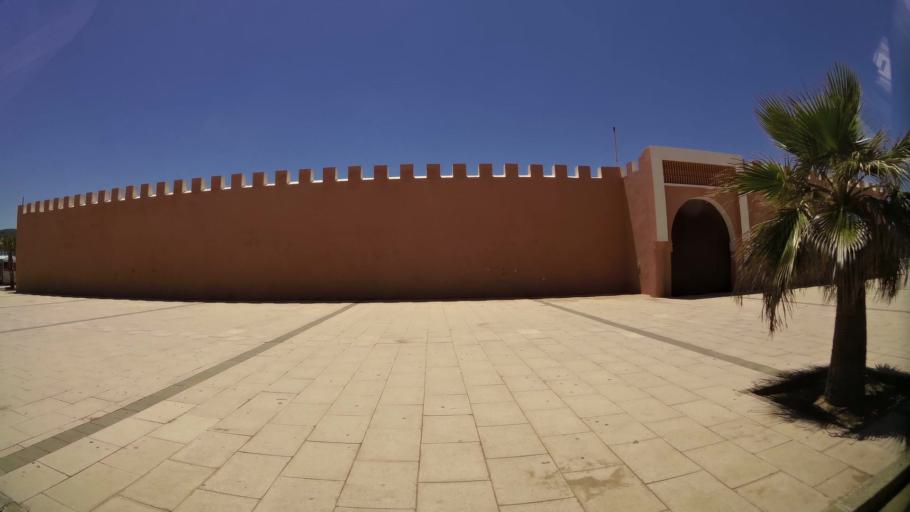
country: MA
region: Oriental
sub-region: Berkane-Taourirt
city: Madagh
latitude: 35.0848
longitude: -2.2165
